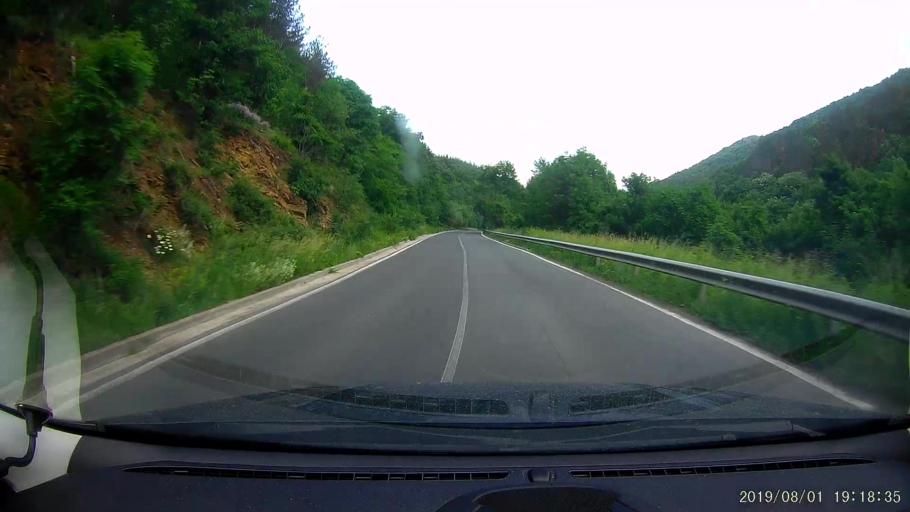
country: BG
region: Shumen
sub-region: Obshtina Smyadovo
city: Smyadovo
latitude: 42.9112
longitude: 26.9397
